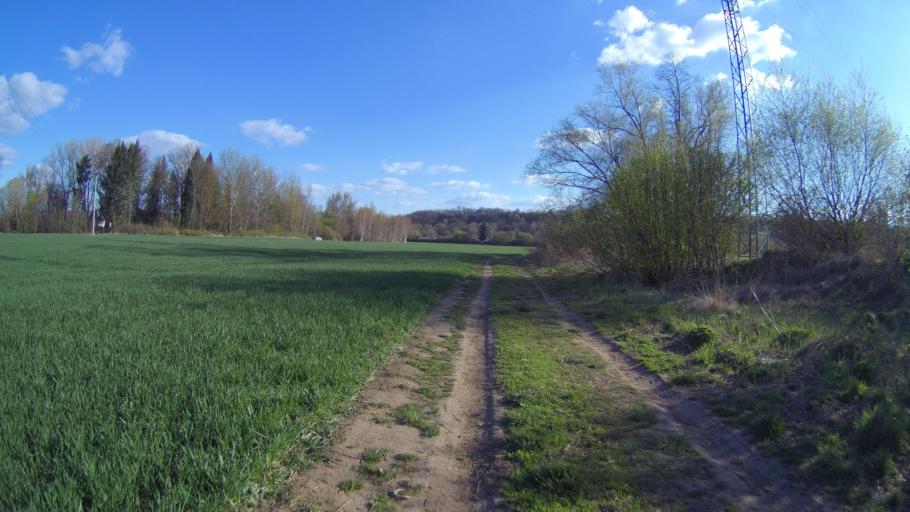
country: CZ
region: Ustecky
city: Zatec
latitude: 50.3266
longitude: 13.5958
